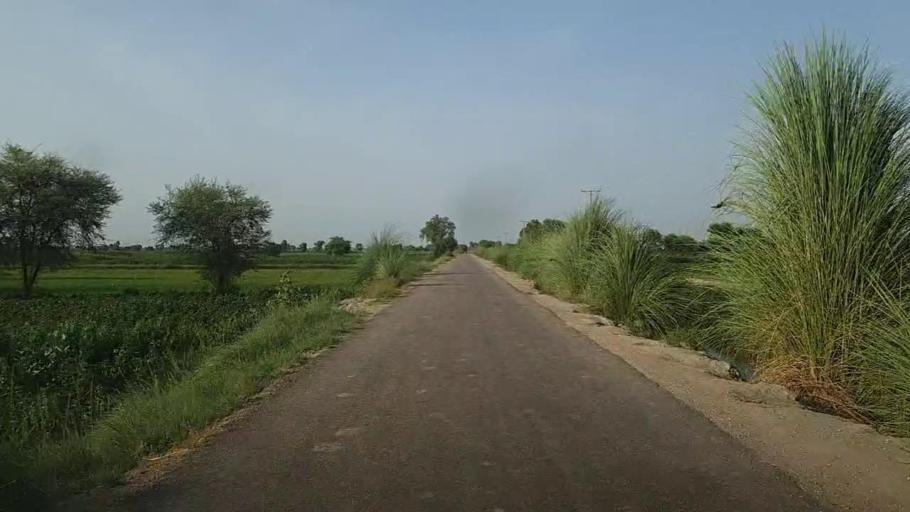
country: PK
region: Sindh
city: Ubauro
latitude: 28.0898
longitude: 69.8189
